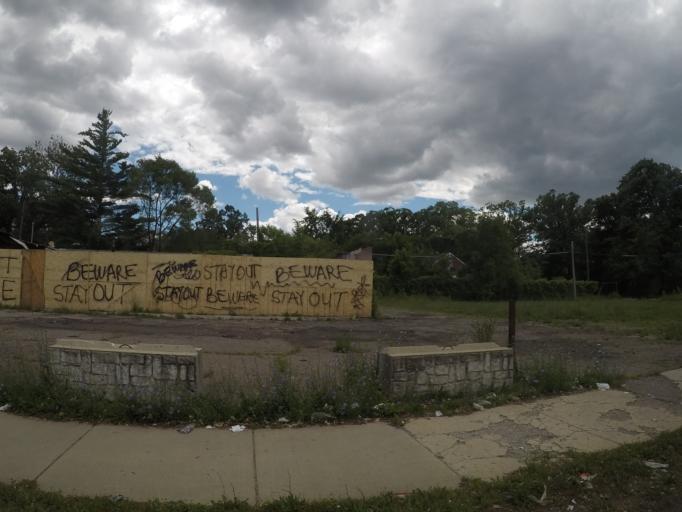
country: US
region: Michigan
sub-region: Wayne County
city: Hamtramck
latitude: 42.4332
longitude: -83.0570
